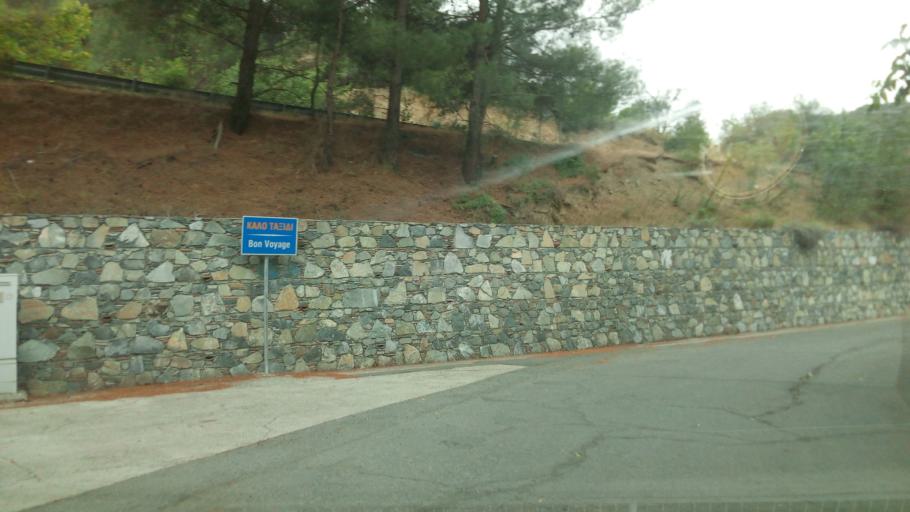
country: CY
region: Limassol
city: Pelendri
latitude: 34.8936
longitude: 33.0079
